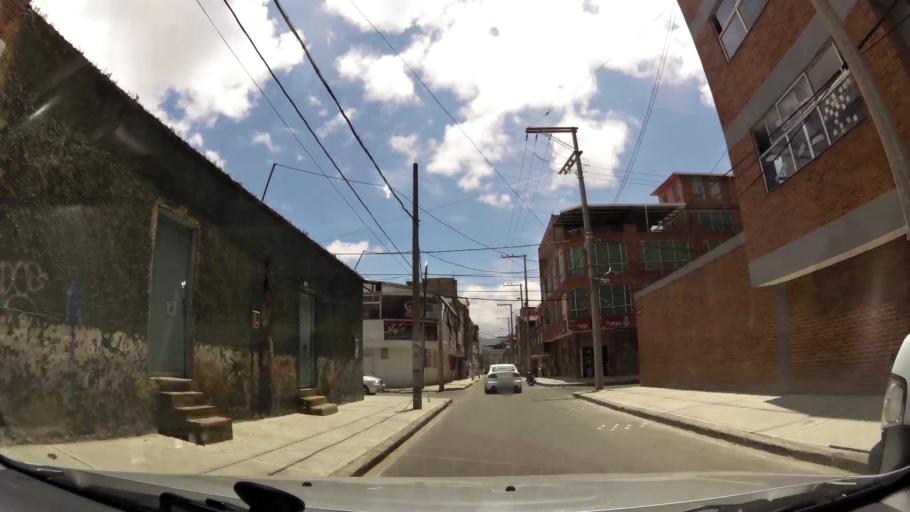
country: CO
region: Bogota D.C.
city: Bogota
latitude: 4.5857
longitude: -74.1076
